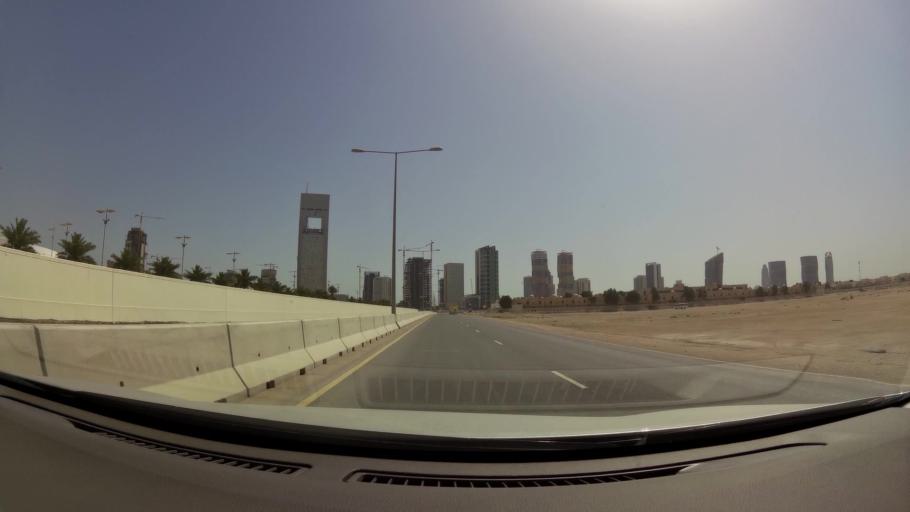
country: QA
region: Baladiyat ad Dawhah
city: Doha
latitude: 25.3898
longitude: 51.5128
